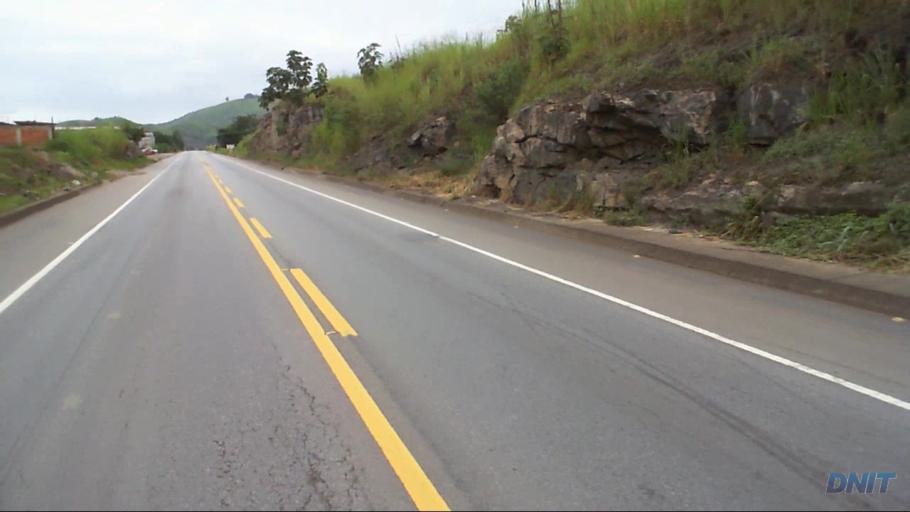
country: BR
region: Minas Gerais
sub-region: Coronel Fabriciano
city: Coronel Fabriciano
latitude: -19.5331
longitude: -42.6236
